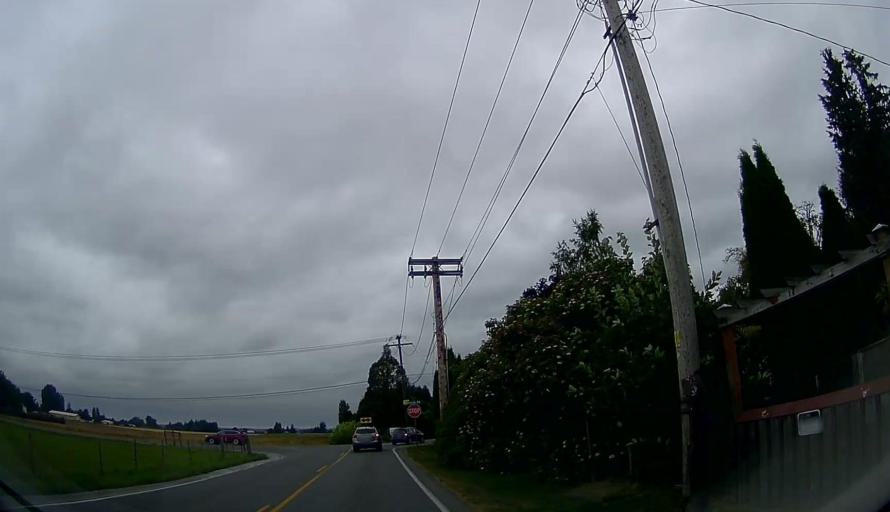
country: US
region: Washington
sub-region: Skagit County
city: Burlington
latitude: 48.4542
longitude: -122.3566
